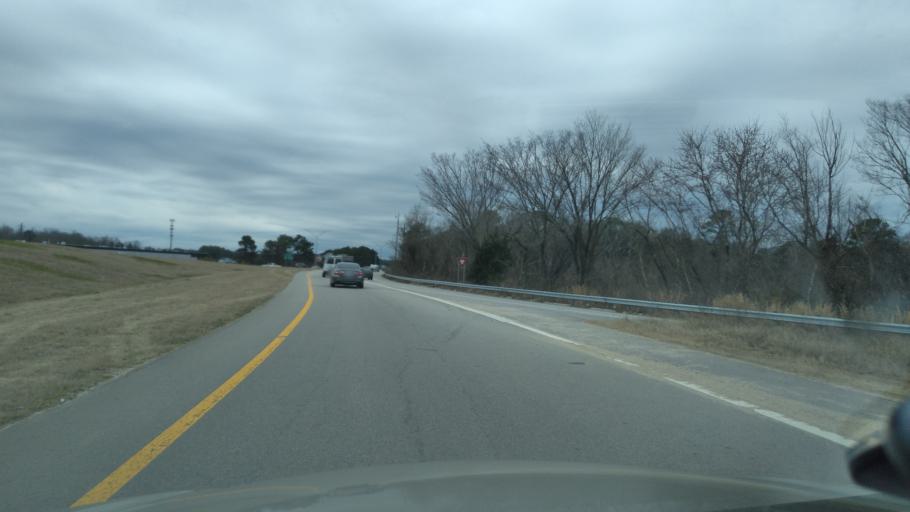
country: US
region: North Carolina
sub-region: Wake County
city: Raleigh
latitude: 35.7553
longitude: -78.6369
